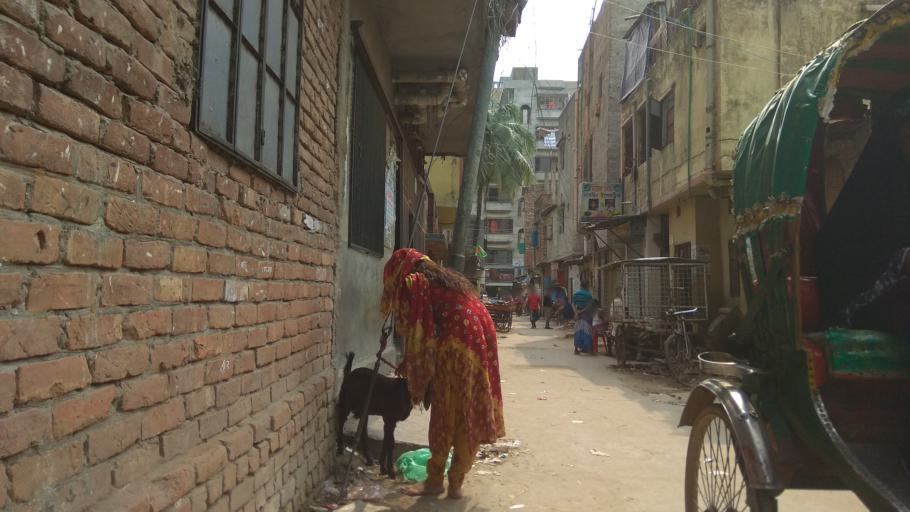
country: BD
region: Dhaka
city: Tungi
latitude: 23.8156
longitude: 90.3720
